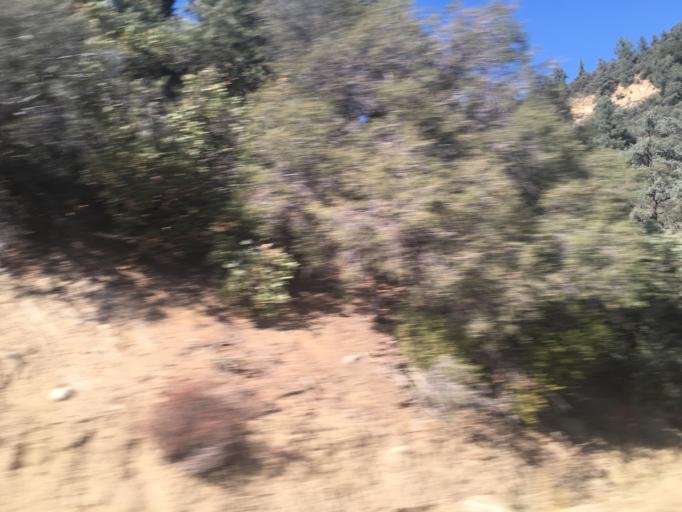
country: US
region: California
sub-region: Ventura County
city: Meiners Oaks
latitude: 34.6485
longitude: -119.3832
